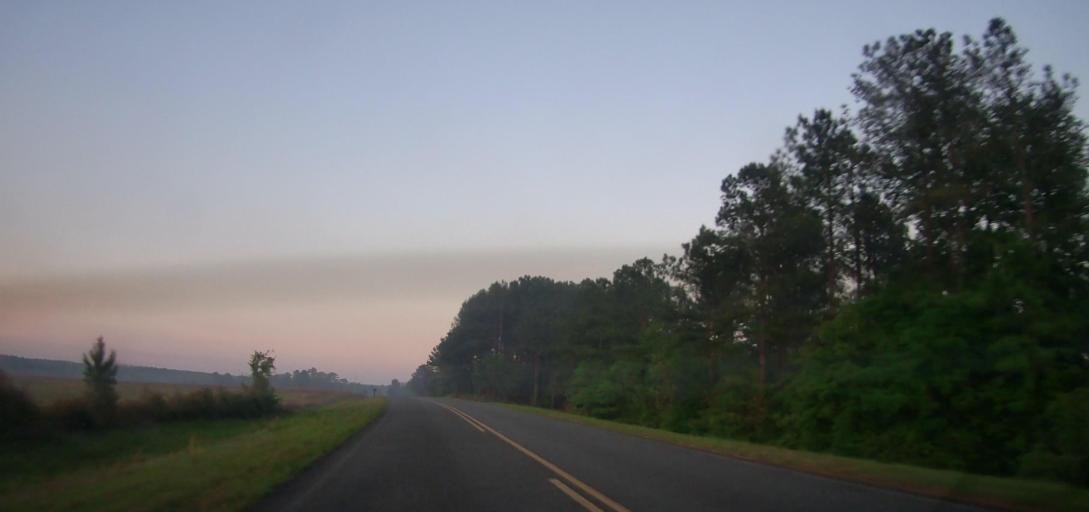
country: US
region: Georgia
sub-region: Marion County
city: Buena Vista
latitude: 32.2622
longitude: -84.5584
